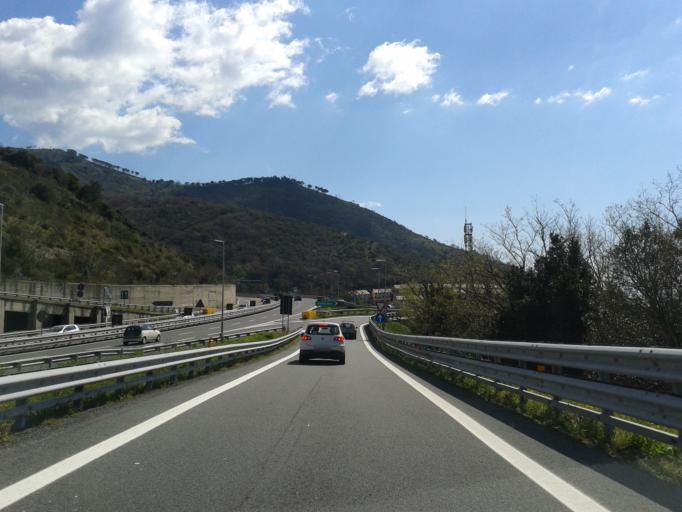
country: IT
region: Liguria
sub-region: Provincia di Genova
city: Bogliasco
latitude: 44.3961
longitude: 9.0081
